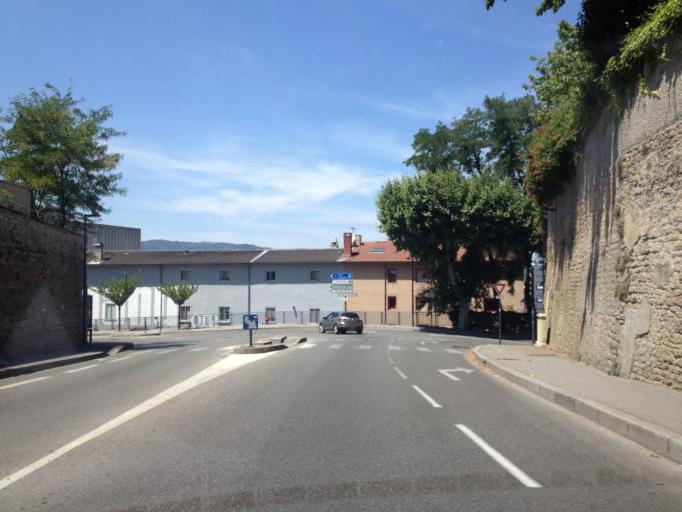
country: FR
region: Rhone-Alpes
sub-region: Departement de la Drome
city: Valence
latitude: 44.9358
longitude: 4.8927
